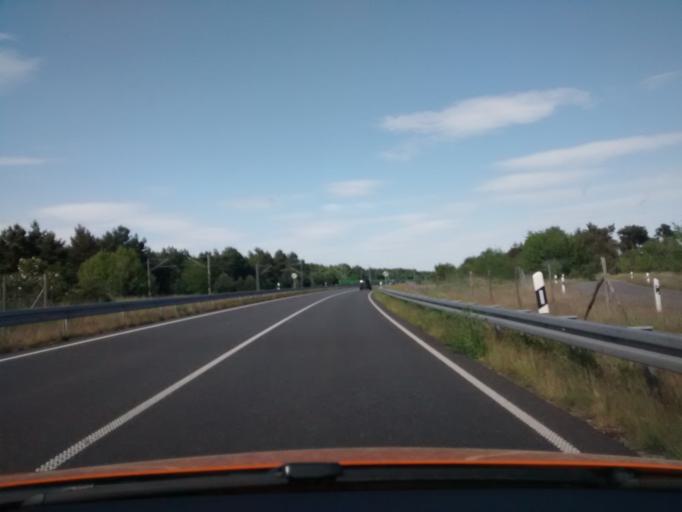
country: DE
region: Brandenburg
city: Luckenwalde
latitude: 52.0591
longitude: 13.1077
